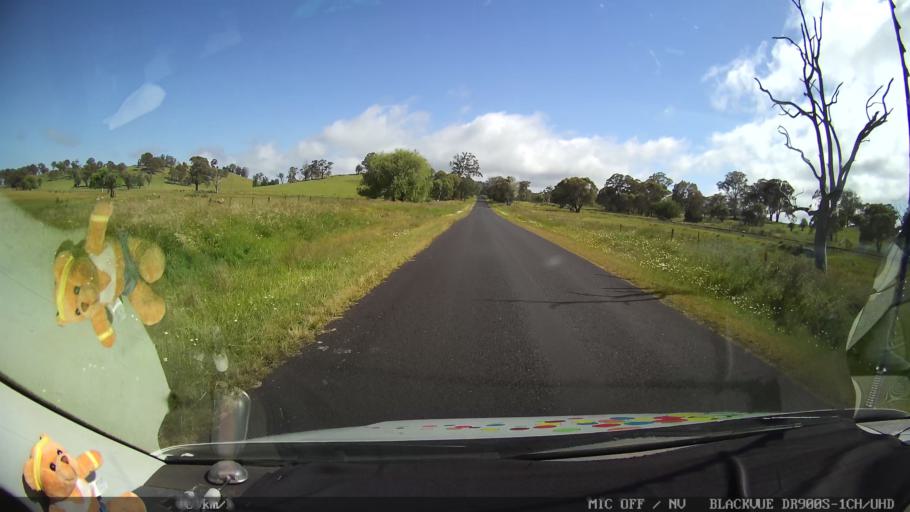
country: AU
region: New South Wales
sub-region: Guyra
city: Guyra
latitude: -30.0434
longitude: 151.6674
